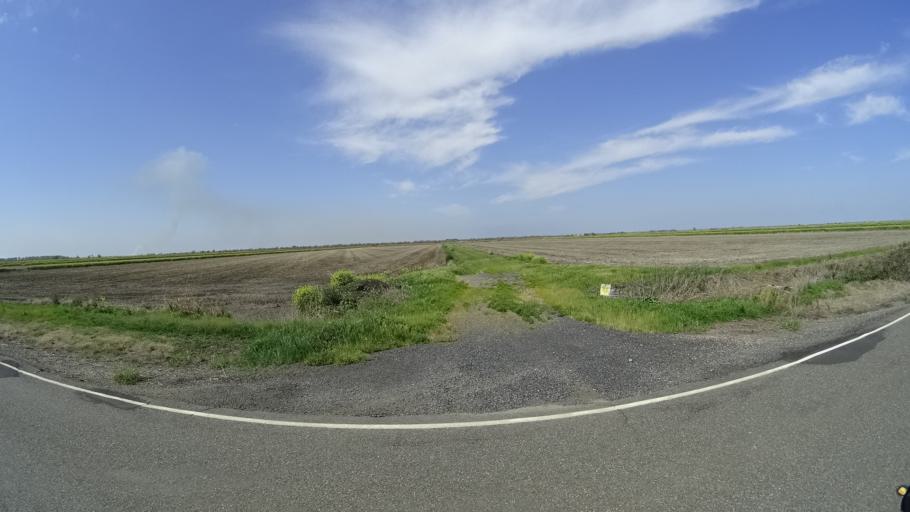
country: US
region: California
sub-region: Butte County
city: Durham
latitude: 39.5443
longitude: -121.8565
